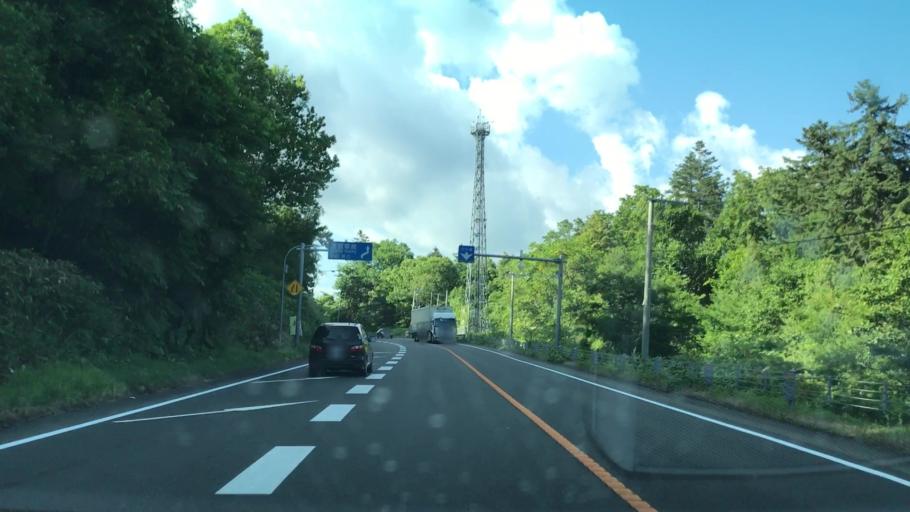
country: JP
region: Hokkaido
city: Shimo-furano
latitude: 42.9055
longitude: 142.4190
